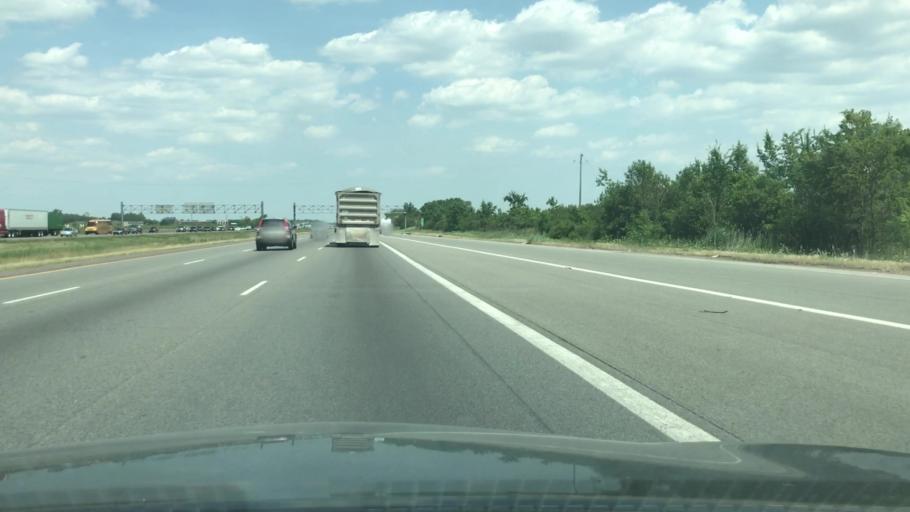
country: US
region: Michigan
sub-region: Wayne County
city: Romulus
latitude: 42.2334
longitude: -83.3634
